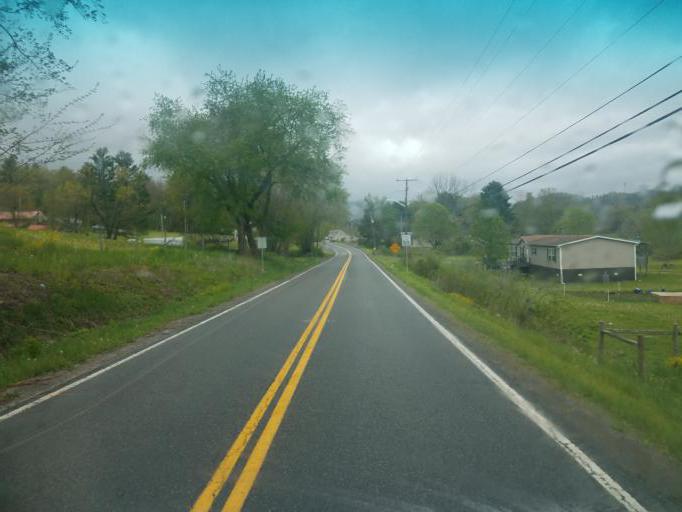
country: US
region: Virginia
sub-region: Bland County
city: Bland
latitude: 37.1661
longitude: -81.1464
